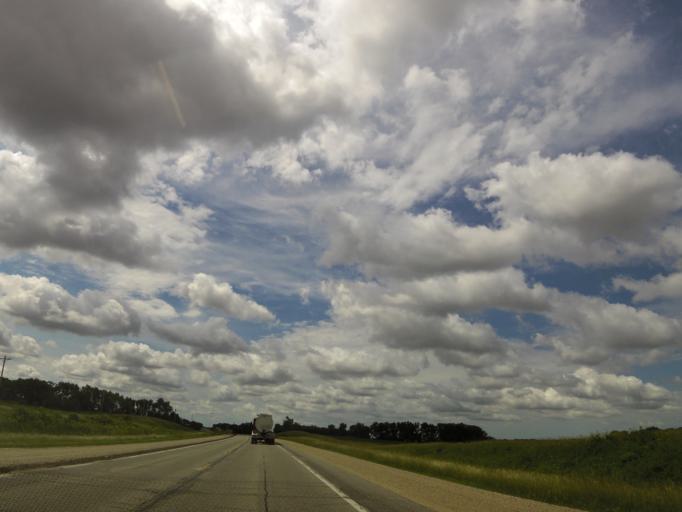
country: US
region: Iowa
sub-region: Howard County
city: Cresco
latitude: 43.2754
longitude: -92.2991
